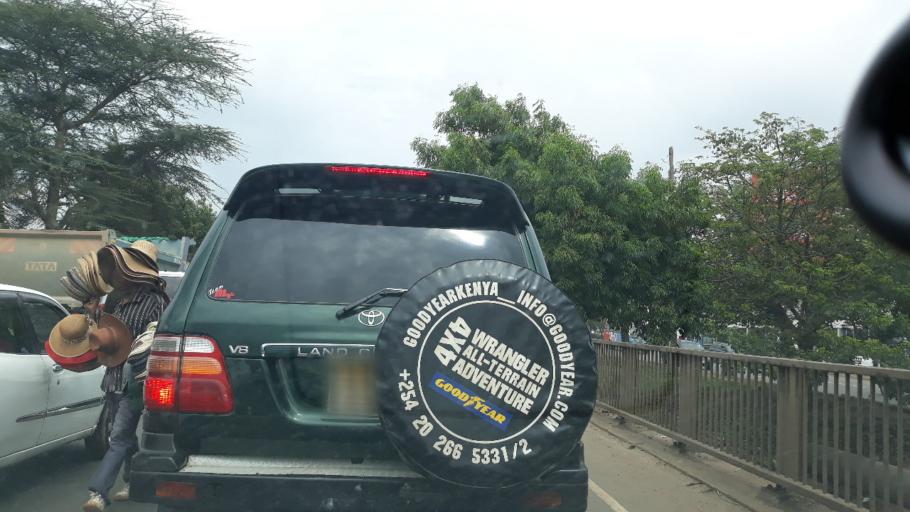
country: KE
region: Nairobi Area
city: Nairobi
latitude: -1.3098
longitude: 36.8287
